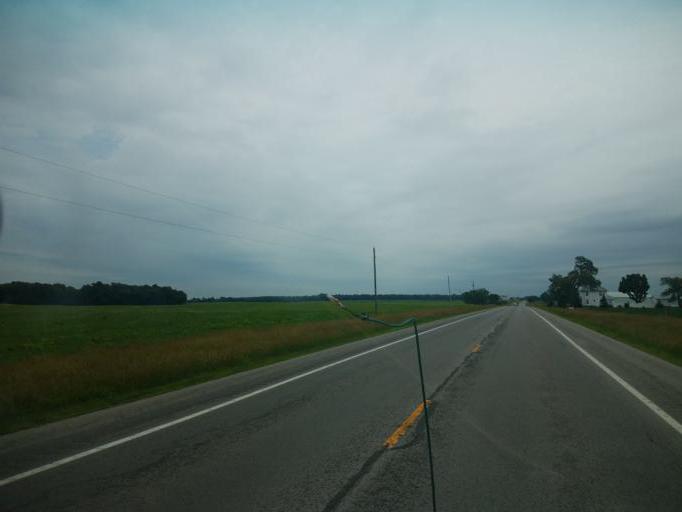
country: US
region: Ohio
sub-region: Hardin County
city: Kenton
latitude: 40.6733
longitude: -83.6653
